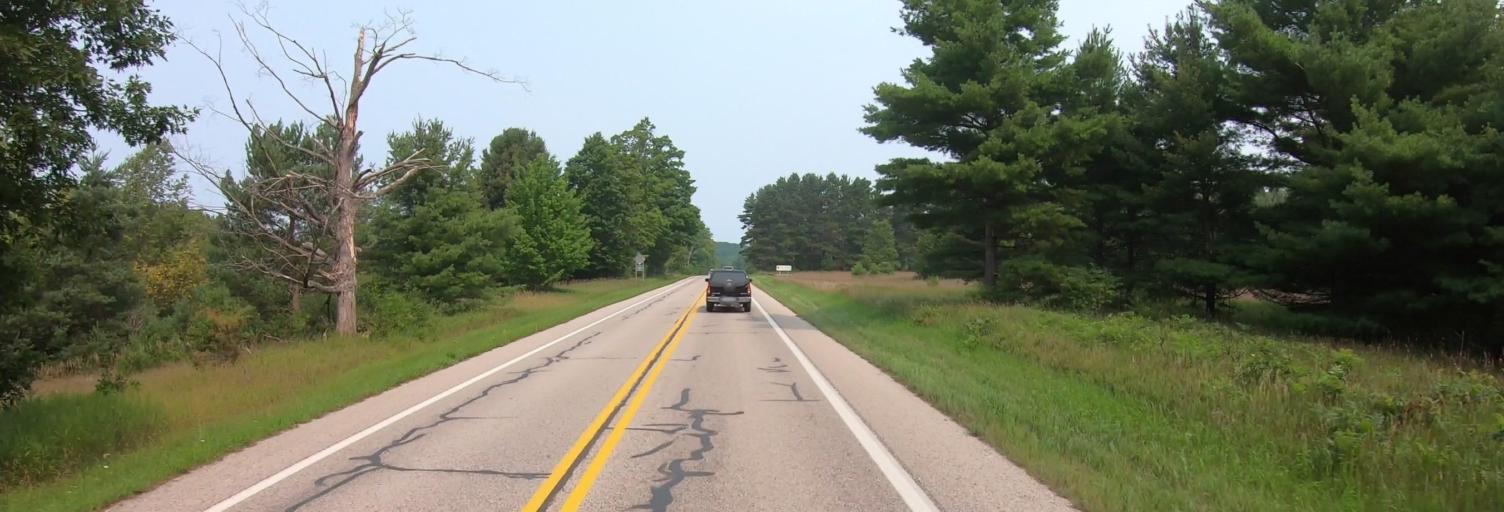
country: US
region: Michigan
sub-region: Leelanau County
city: Leland
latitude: 44.9280
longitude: -85.9472
